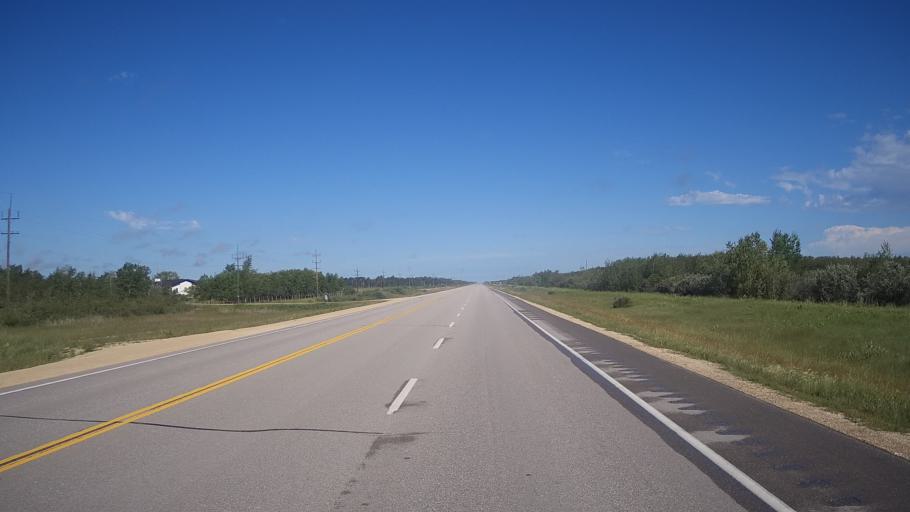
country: CA
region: Manitoba
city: Stonewall
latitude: 50.2259
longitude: -97.6912
